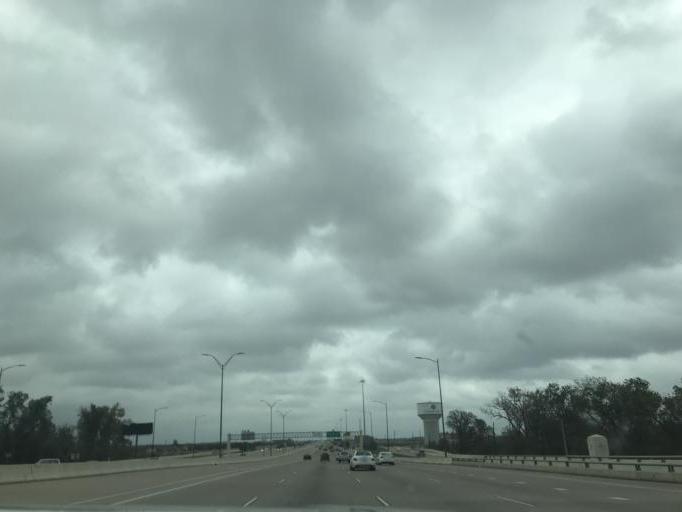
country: US
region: Texas
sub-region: Fort Bend County
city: Greatwood
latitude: 29.5687
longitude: -95.6670
